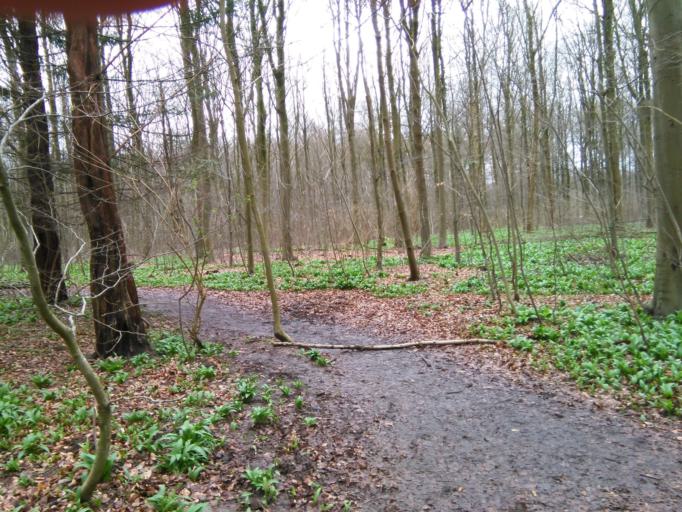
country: DK
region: Central Jutland
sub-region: Arhus Kommune
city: Arhus
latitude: 56.1815
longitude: 10.2214
